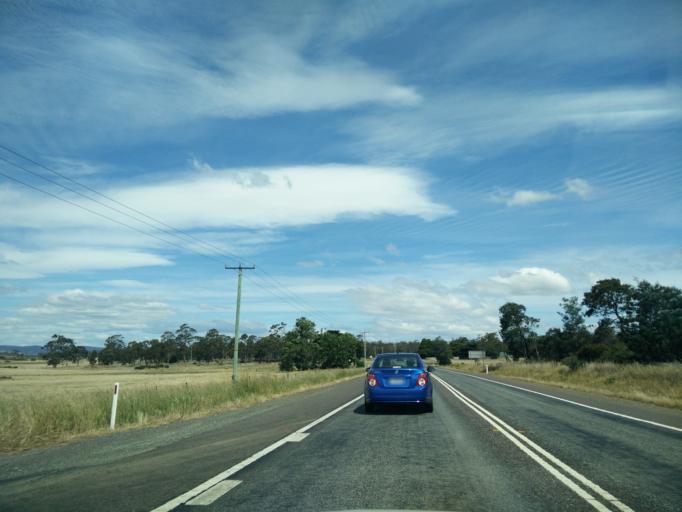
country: AU
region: Tasmania
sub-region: Northern Midlands
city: Evandale
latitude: -41.7773
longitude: 147.3717
